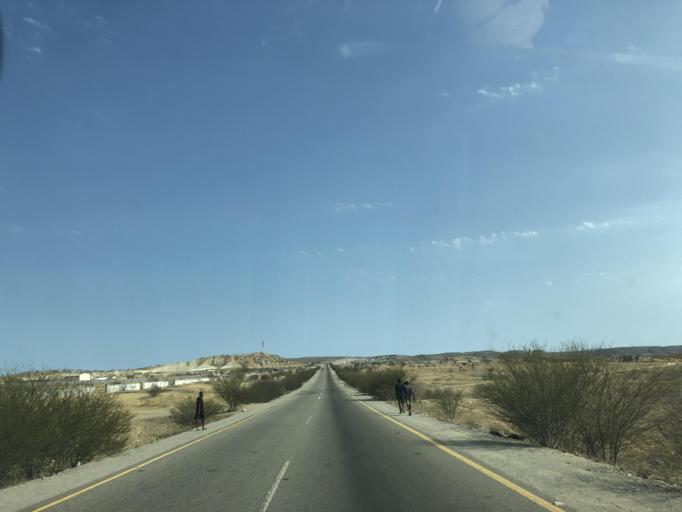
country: AO
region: Benguela
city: Benguela
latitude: -12.7386
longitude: 13.3506
